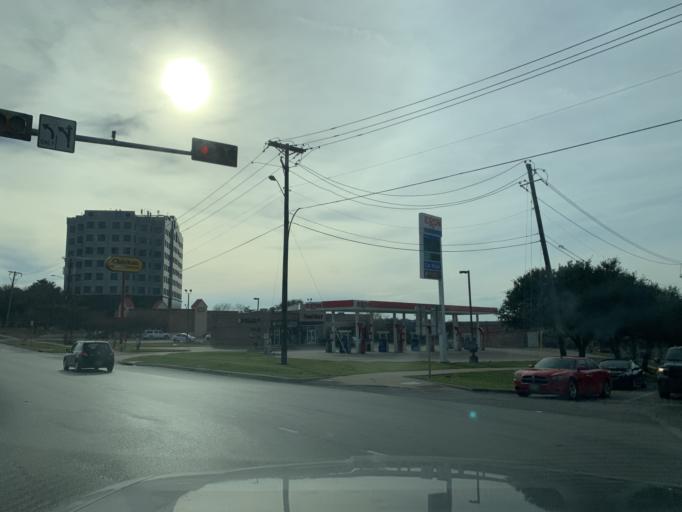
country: US
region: Texas
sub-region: Tarrant County
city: Euless
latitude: 32.7934
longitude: -97.0575
